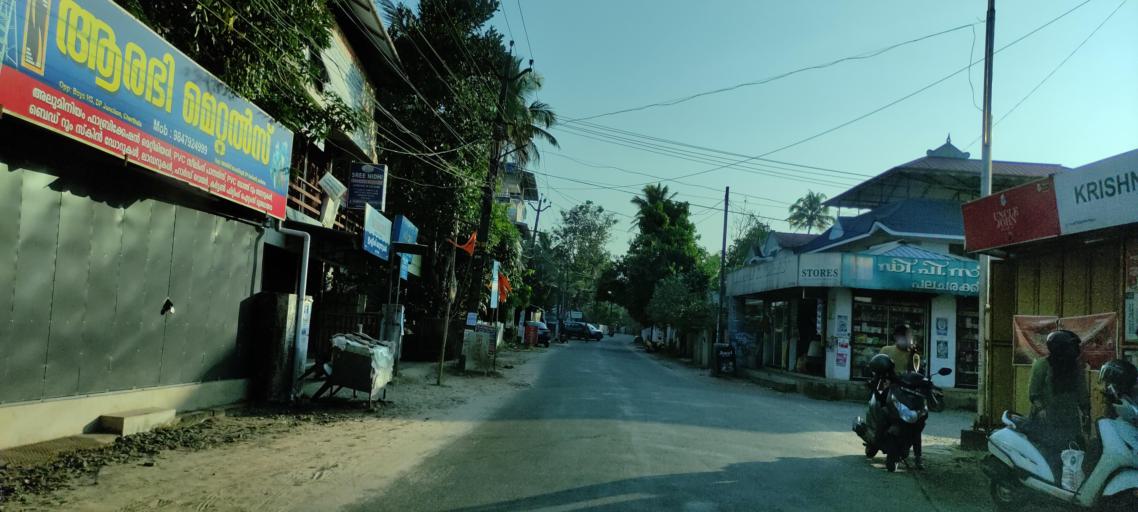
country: IN
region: Kerala
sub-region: Alappuzha
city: Shertallai
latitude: 9.6806
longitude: 76.3433
